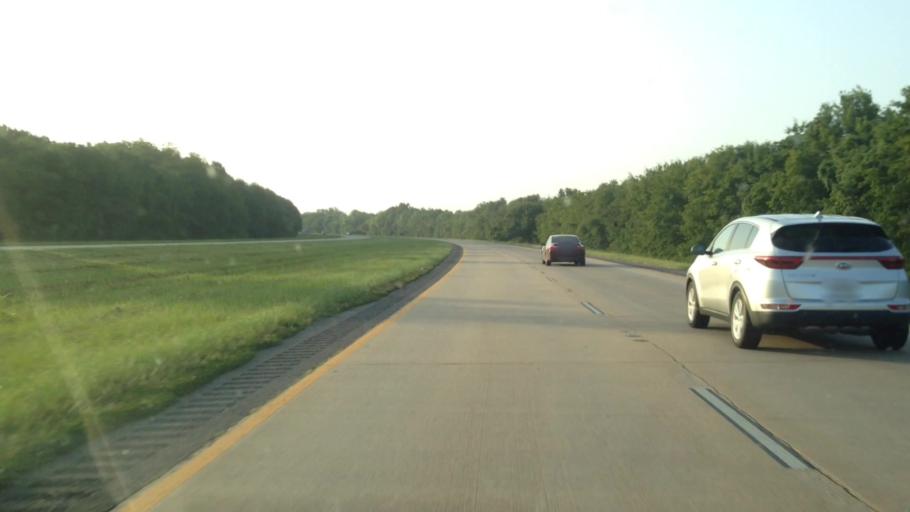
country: US
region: Louisiana
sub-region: Natchitoches Parish
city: Vienna Bend
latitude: 31.5735
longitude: -93.0174
